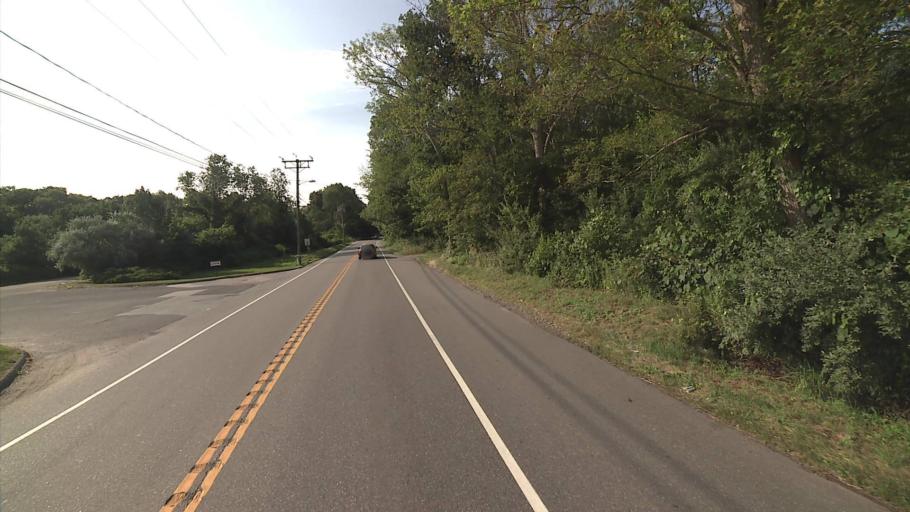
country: US
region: Connecticut
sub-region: New London County
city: Pawcatuck
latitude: 41.4275
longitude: -71.8623
